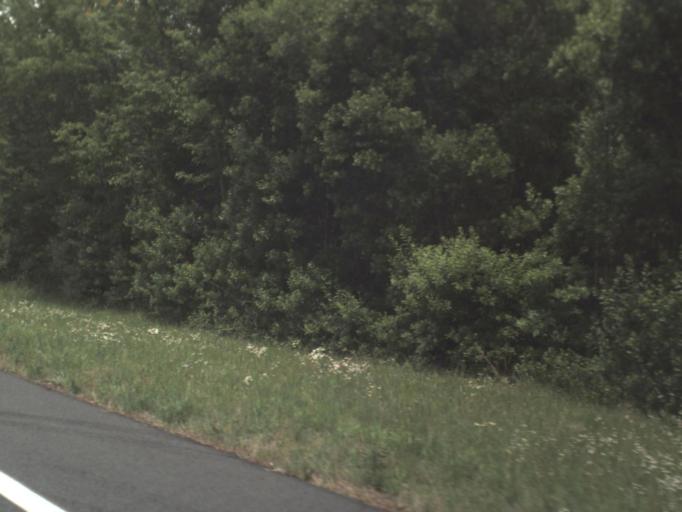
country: US
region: Florida
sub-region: Hamilton County
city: Jasper
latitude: 30.5631
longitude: -82.6804
